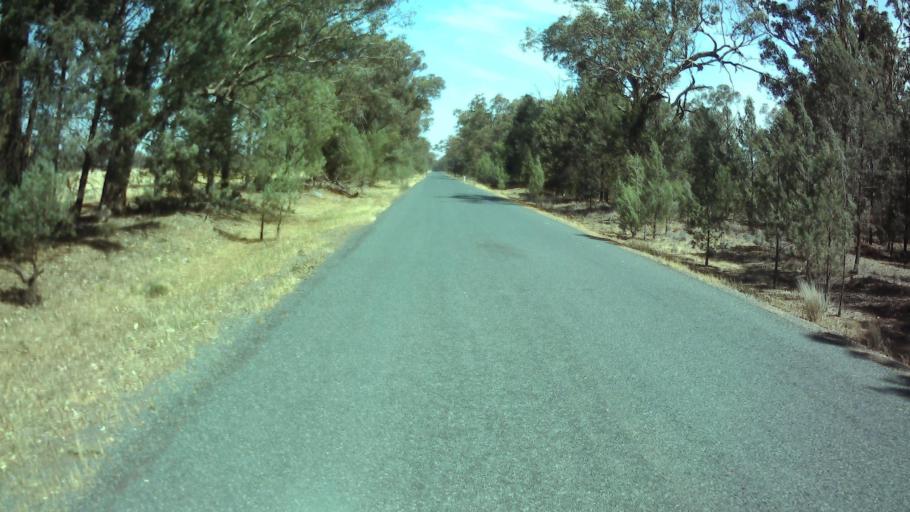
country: AU
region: New South Wales
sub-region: Weddin
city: Grenfell
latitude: -34.0597
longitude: 148.1322
